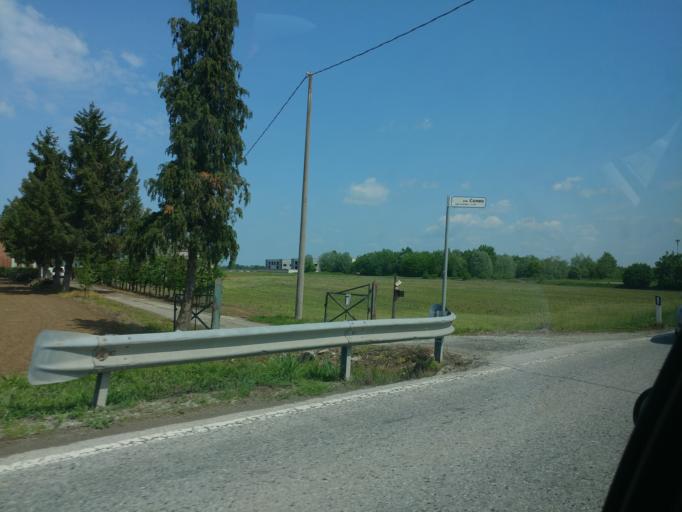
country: IT
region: Piedmont
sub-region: Provincia di Cuneo
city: Carde
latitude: 44.7373
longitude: 7.4175
